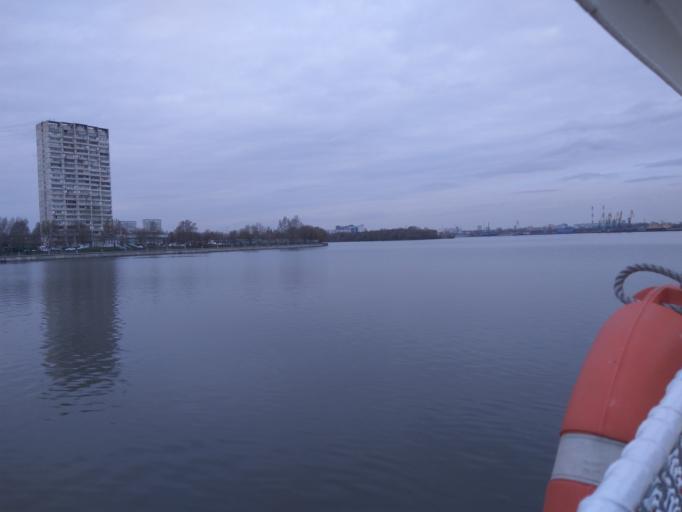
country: RU
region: Moscow
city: Mar'ino
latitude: 55.6833
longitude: 37.7131
